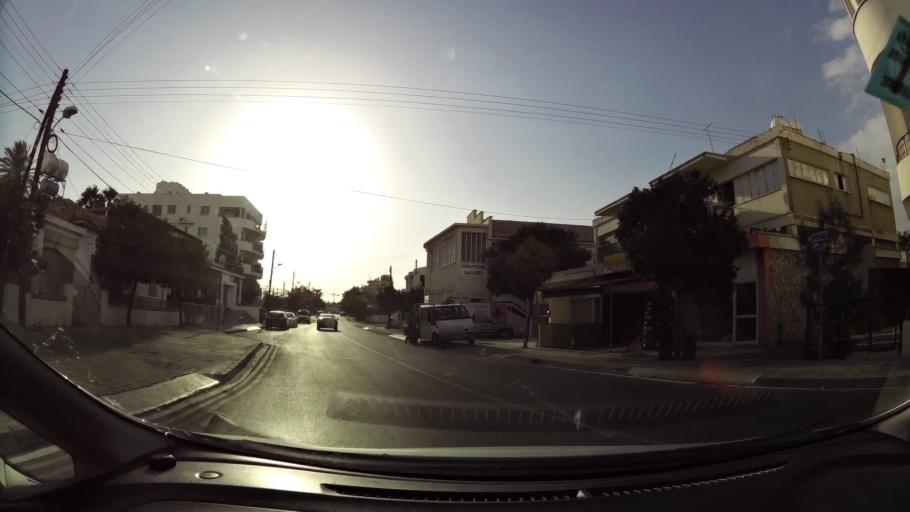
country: CY
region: Lefkosia
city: Nicosia
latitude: 35.1745
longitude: 33.3762
